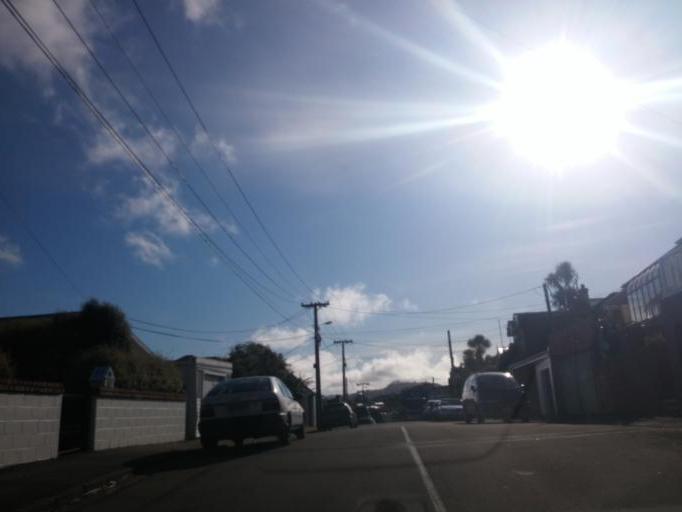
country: NZ
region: Wellington
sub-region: Wellington City
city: Brooklyn
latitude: -41.3081
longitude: 174.7644
